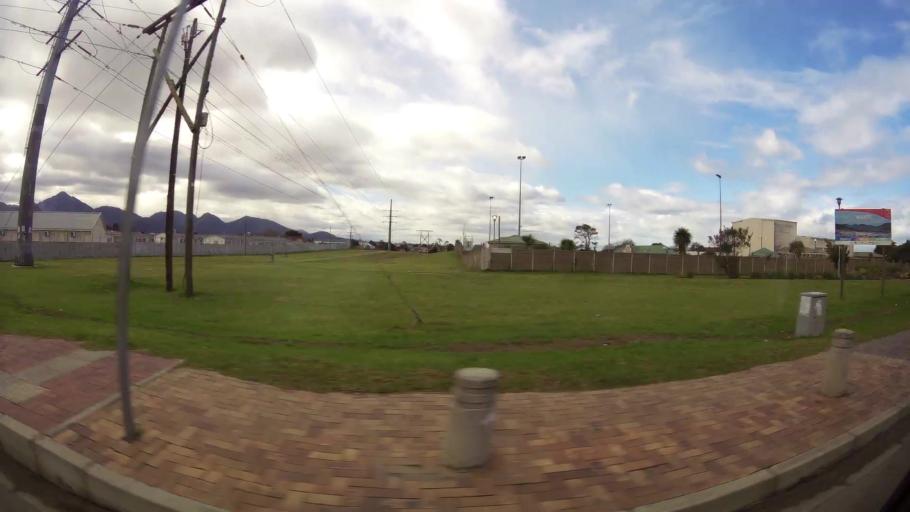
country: ZA
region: Western Cape
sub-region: Eden District Municipality
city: George
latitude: -33.9813
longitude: 22.4721
